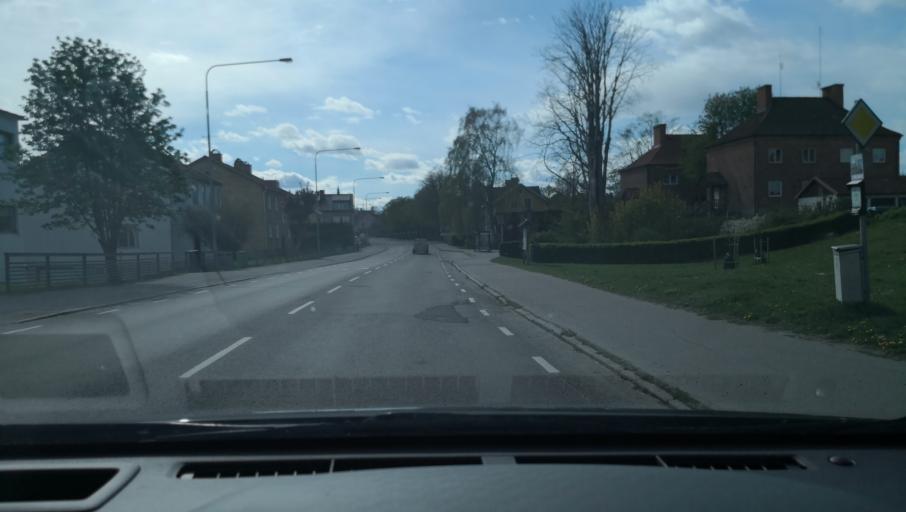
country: SE
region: OErebro
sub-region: Hallsbergs Kommun
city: Hallsberg
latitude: 59.0642
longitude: 15.0994
